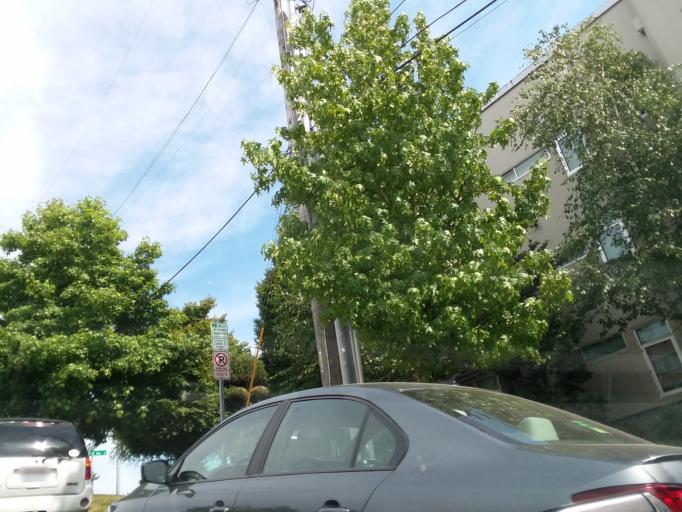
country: US
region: Washington
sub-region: King County
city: Seattle
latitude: 47.6456
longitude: -122.3238
